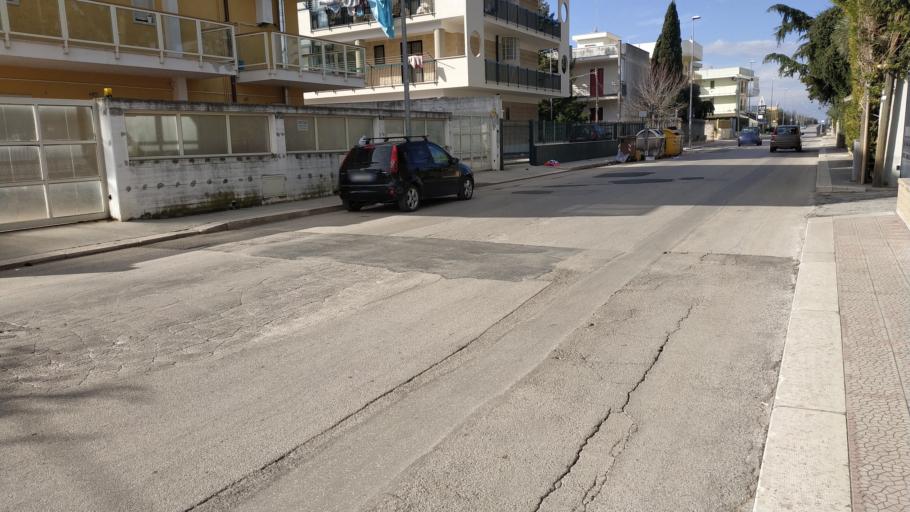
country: IT
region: Apulia
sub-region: Provincia di Bari
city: Bitonto
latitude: 41.1105
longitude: 16.6787
